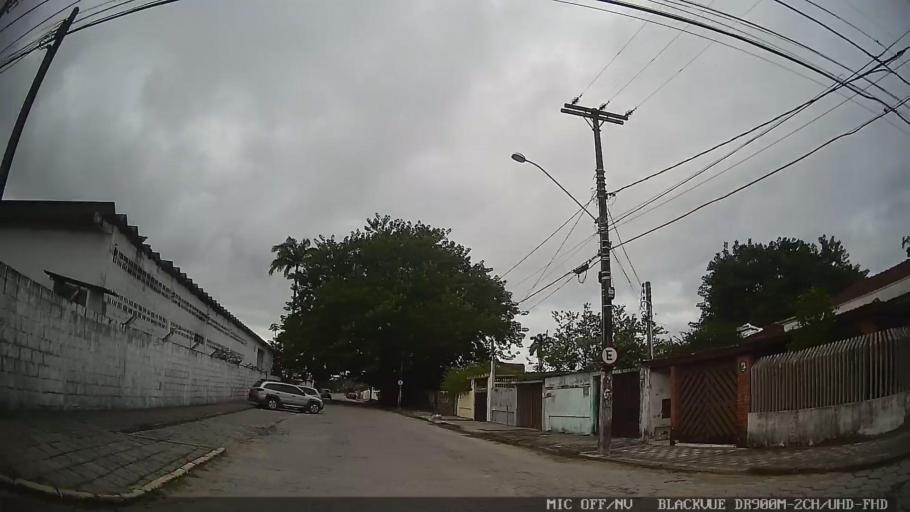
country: BR
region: Sao Paulo
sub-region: Itanhaem
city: Itanhaem
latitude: -24.1909
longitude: -46.8110
